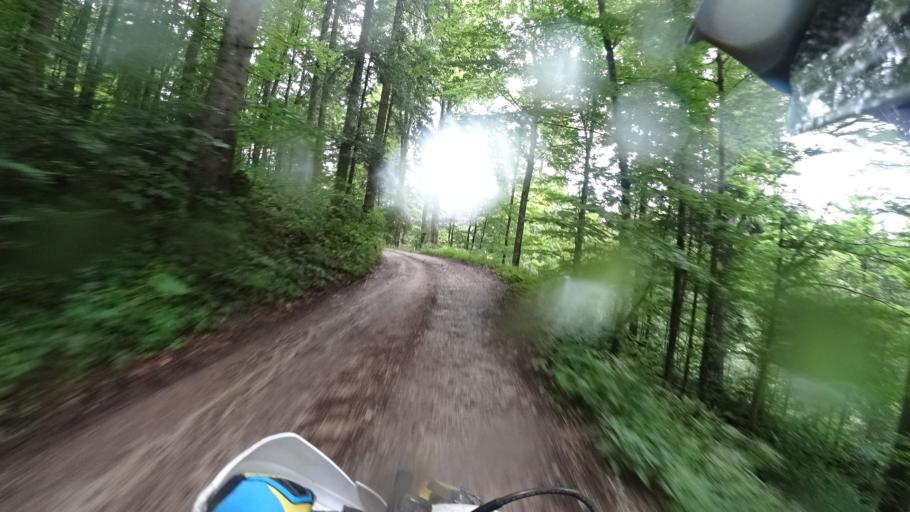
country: HR
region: Primorsko-Goranska
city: Vrbovsko
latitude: 45.2970
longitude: 14.9577
